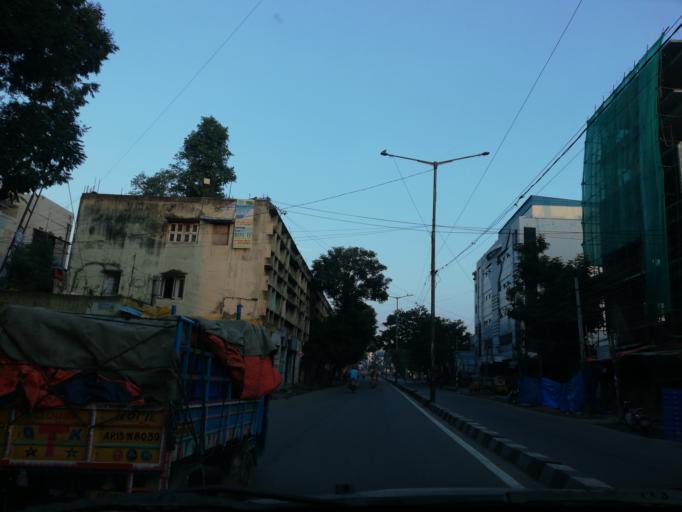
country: IN
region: Telangana
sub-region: Rangareddi
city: Gaddi Annaram
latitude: 17.3951
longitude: 78.4981
